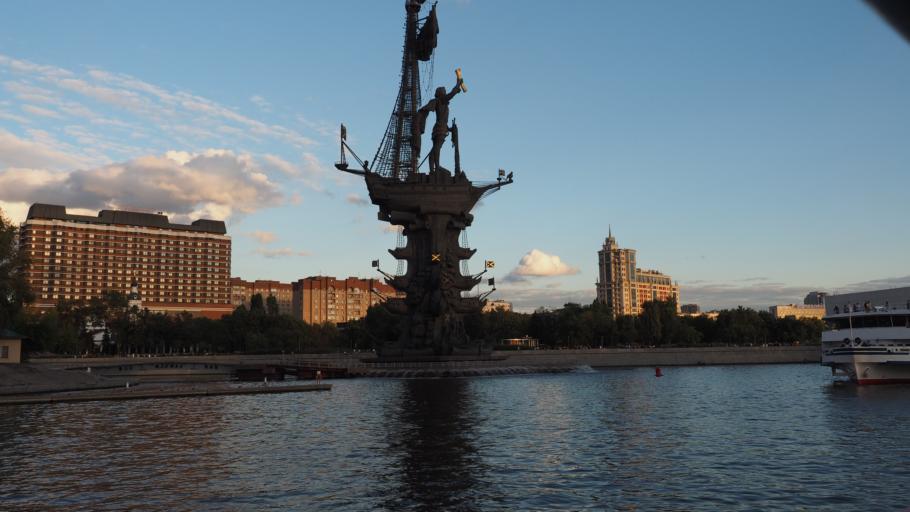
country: RU
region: Moscow
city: Moscow
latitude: 55.7399
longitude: 37.6070
